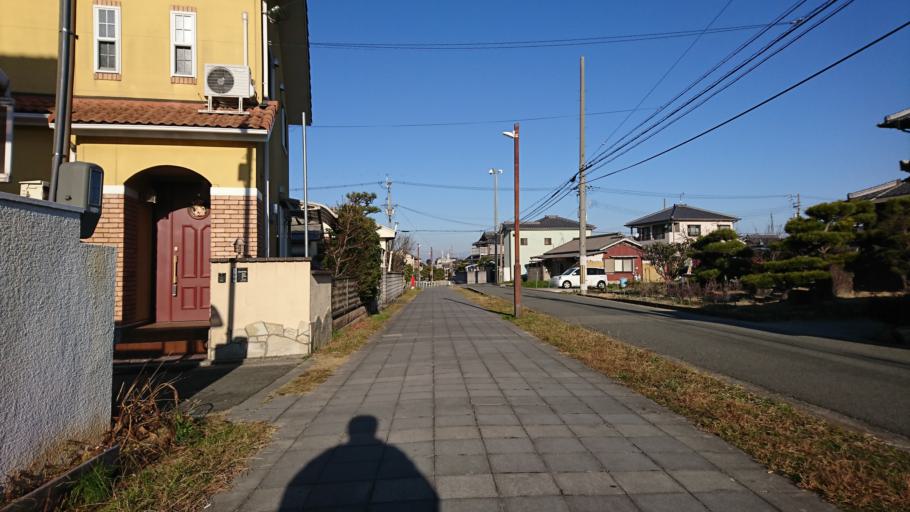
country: JP
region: Hyogo
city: Kakogawacho-honmachi
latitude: 34.7440
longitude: 134.8438
